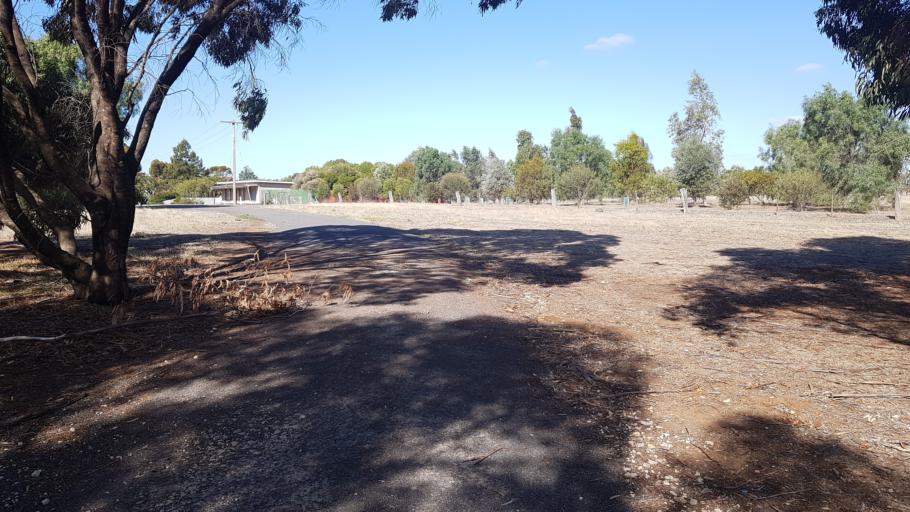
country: AU
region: Victoria
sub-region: Horsham
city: Horsham
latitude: -36.7460
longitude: 141.9384
